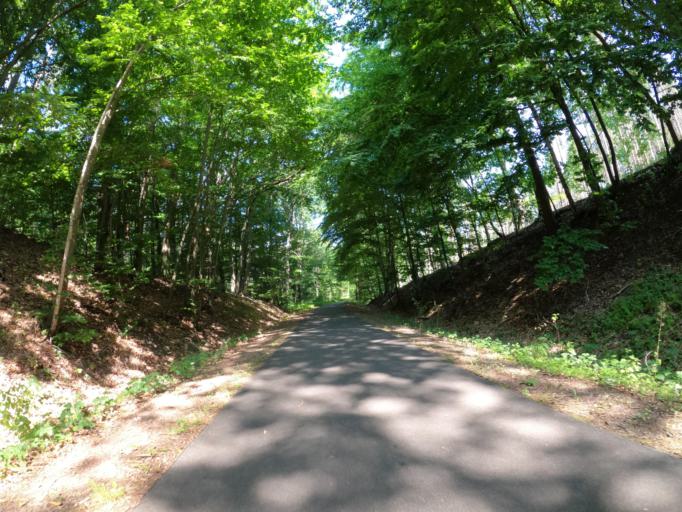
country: DE
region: Brandenburg
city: Templin
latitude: 53.2322
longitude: 13.5019
